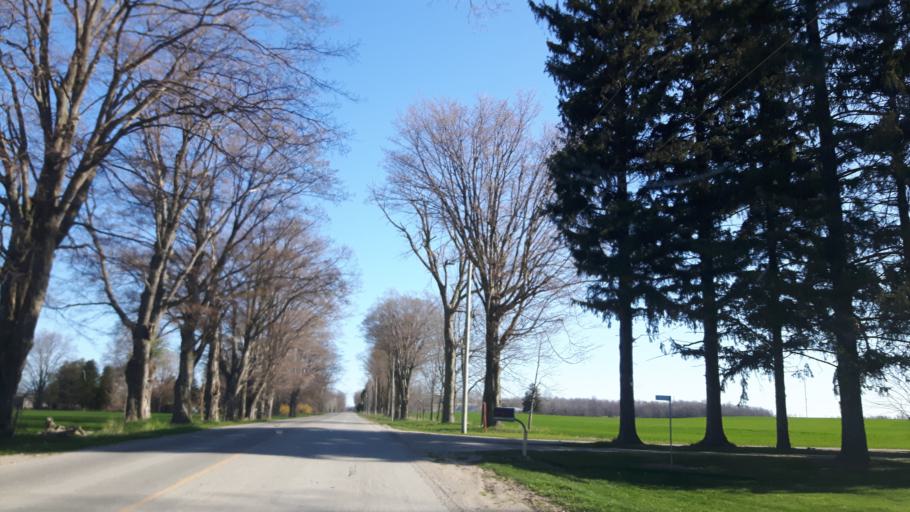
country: CA
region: Ontario
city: Goderich
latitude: 43.7040
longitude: -81.6849
